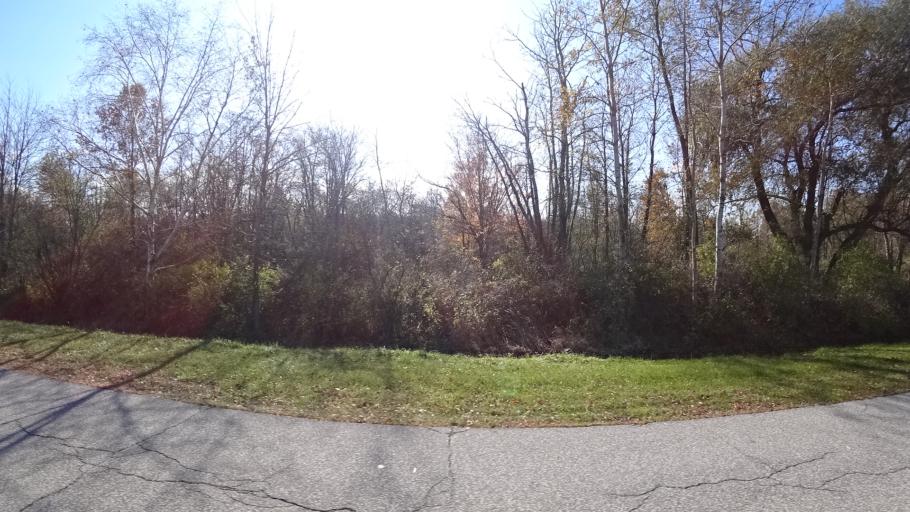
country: US
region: Indiana
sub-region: LaPorte County
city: Long Beach
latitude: 41.7329
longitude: -86.8297
